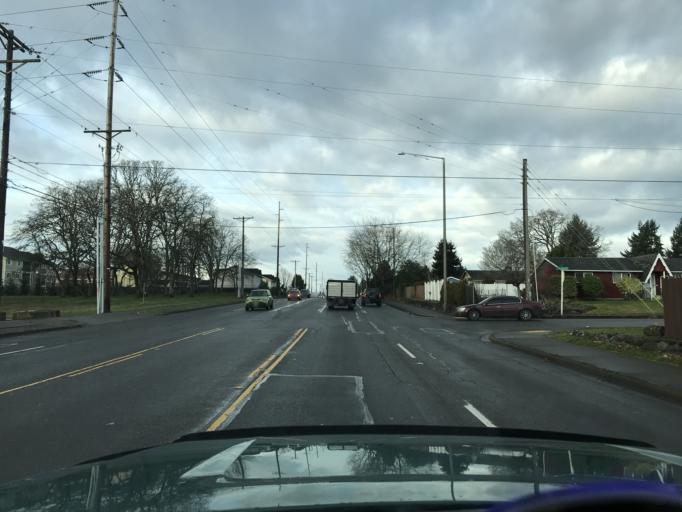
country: US
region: Washington
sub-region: Pierce County
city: Lakewood
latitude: 47.1906
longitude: -122.4937
